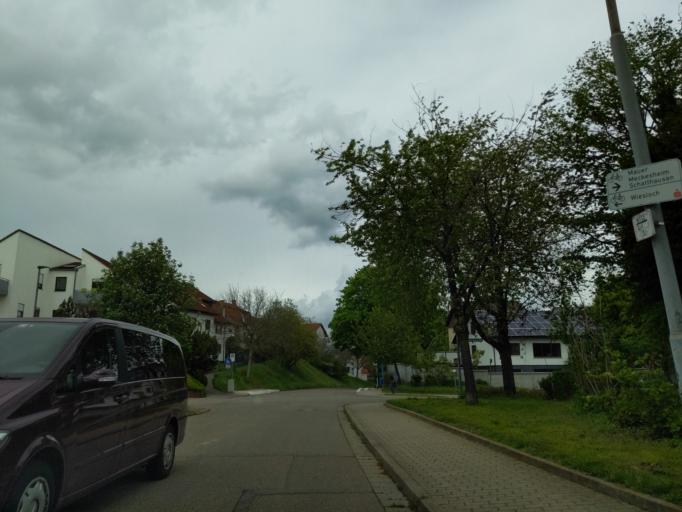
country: DE
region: Baden-Wuerttemberg
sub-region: Karlsruhe Region
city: Dielheim
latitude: 49.2960
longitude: 8.7369
